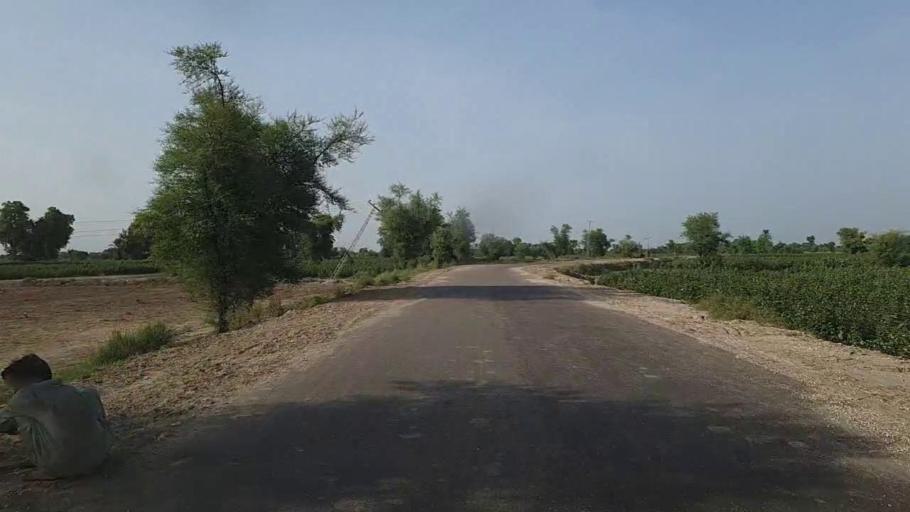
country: PK
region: Sindh
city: Ubauro
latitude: 28.1066
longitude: 69.8476
